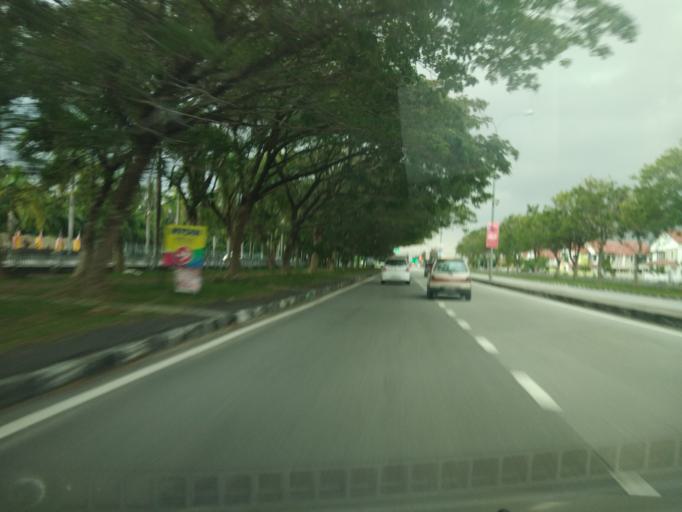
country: MY
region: Penang
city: Tasek Glugor
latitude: 5.5196
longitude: 100.4734
